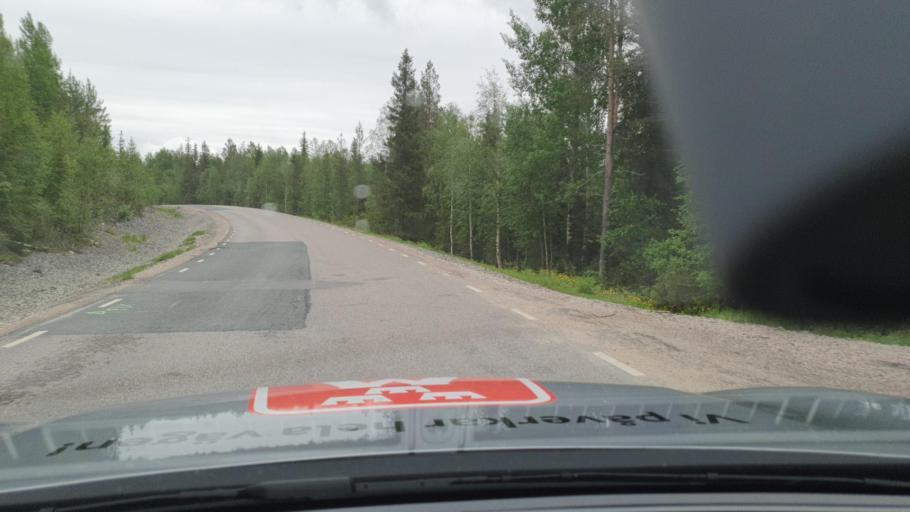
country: SE
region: Norrbotten
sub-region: Overtornea Kommun
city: OEvertornea
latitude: 66.5143
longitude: 23.3843
